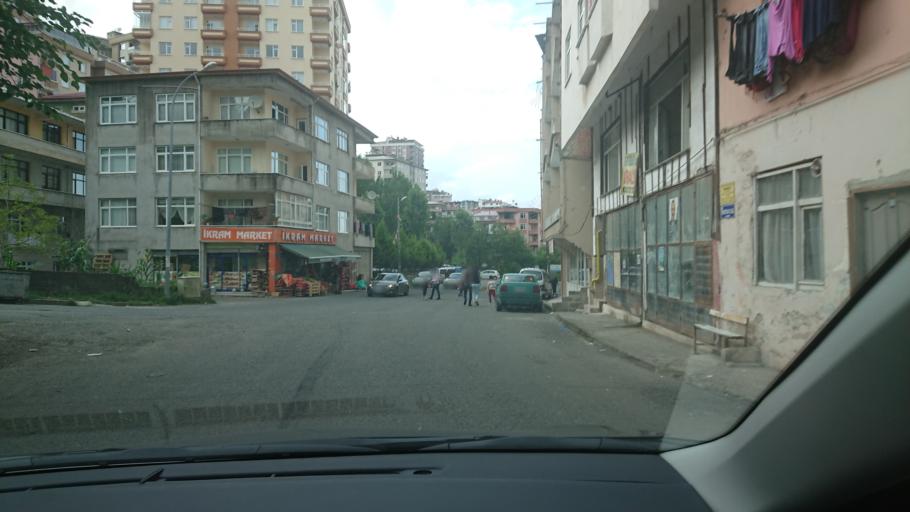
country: TR
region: Rize
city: Rize
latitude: 41.0181
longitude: 40.5160
